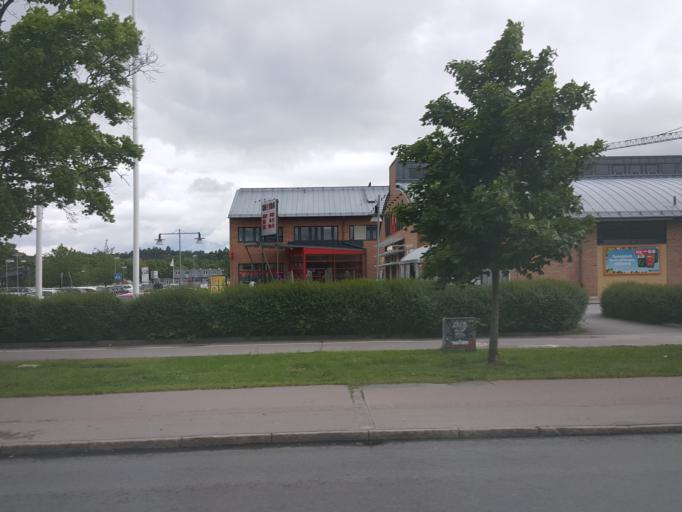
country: SE
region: Uppsala
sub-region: Uppsala Kommun
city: Uppsala
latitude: 59.8499
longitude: 17.6594
